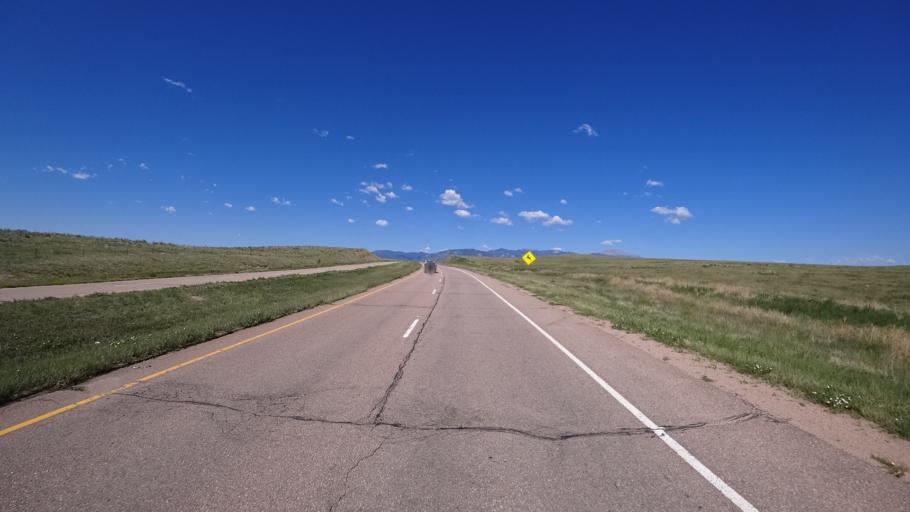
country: US
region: Colorado
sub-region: El Paso County
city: Security-Widefield
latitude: 38.7622
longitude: -104.6749
